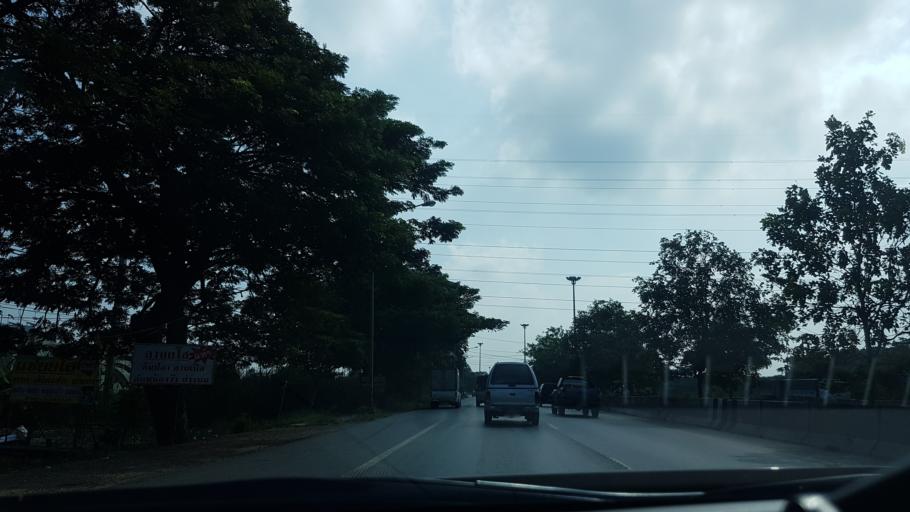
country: TH
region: Phra Nakhon Si Ayutthaya
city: Bang Pa-in
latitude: 14.1700
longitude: 100.6118
